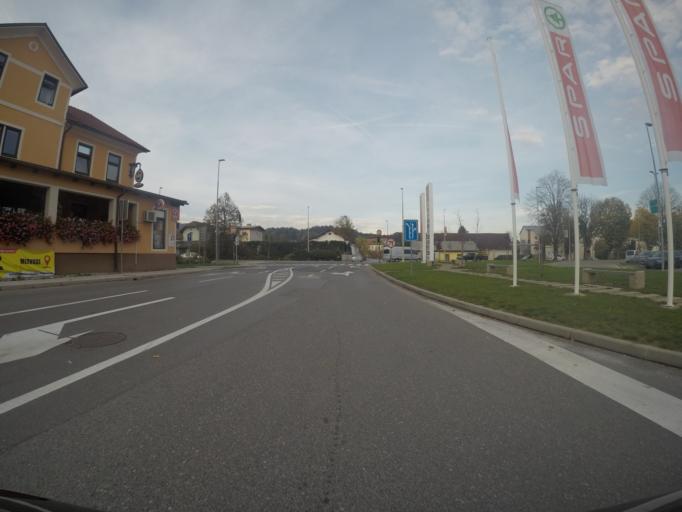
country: SI
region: Medvode
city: Medvode
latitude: 46.1399
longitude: 14.4139
